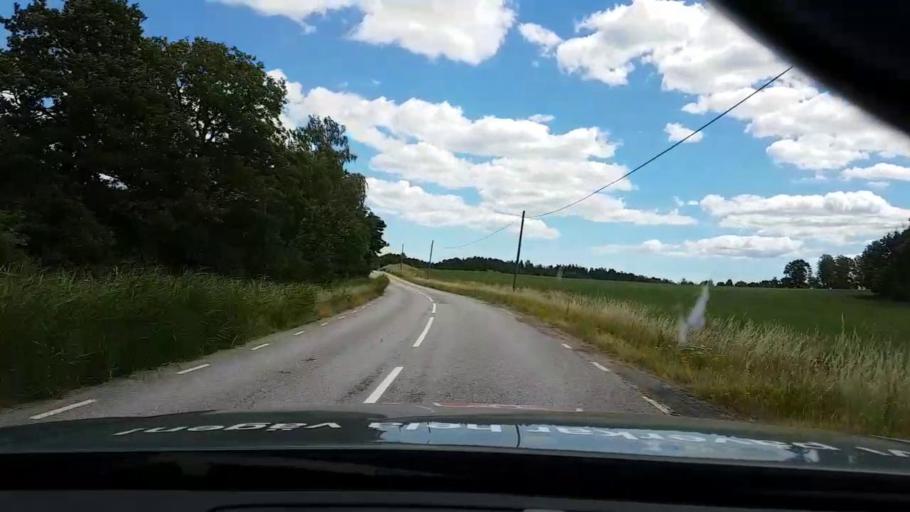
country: SE
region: Kalmar
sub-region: Vasterviks Kommun
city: Forserum
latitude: 58.0417
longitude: 16.4236
